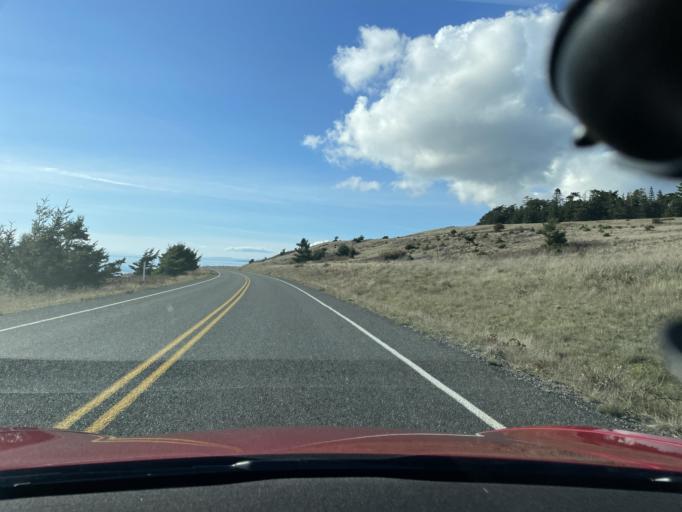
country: US
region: Washington
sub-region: San Juan County
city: Friday Harbor
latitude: 48.4570
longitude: -122.9852
